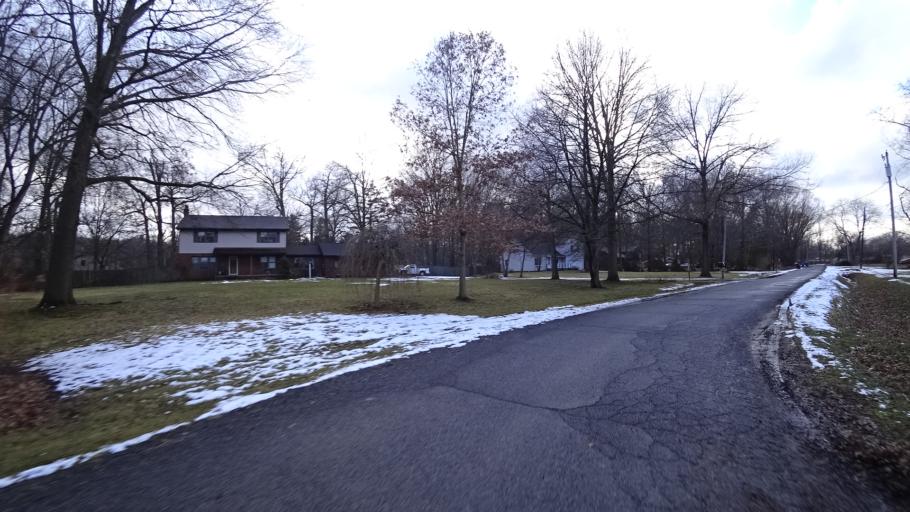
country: US
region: Indiana
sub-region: Porter County
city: Porter
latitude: 41.6105
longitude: -87.0883
